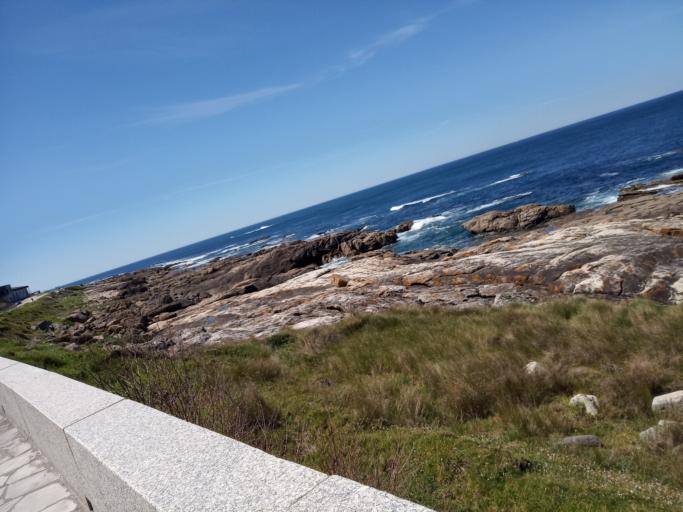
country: ES
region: Galicia
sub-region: Provincia de Pontevedra
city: A Guarda
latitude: 41.8903
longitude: -8.8802
